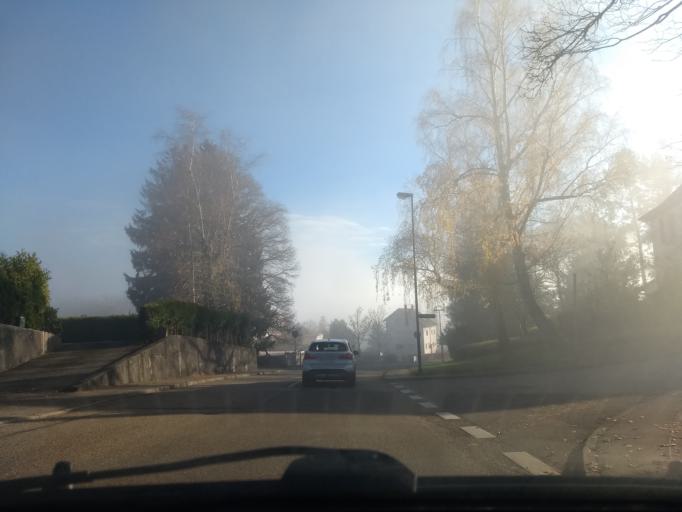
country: DE
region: Baden-Wuerttemberg
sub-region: Karlsruhe Region
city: Baden-Baden
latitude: 48.7778
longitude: 8.2717
